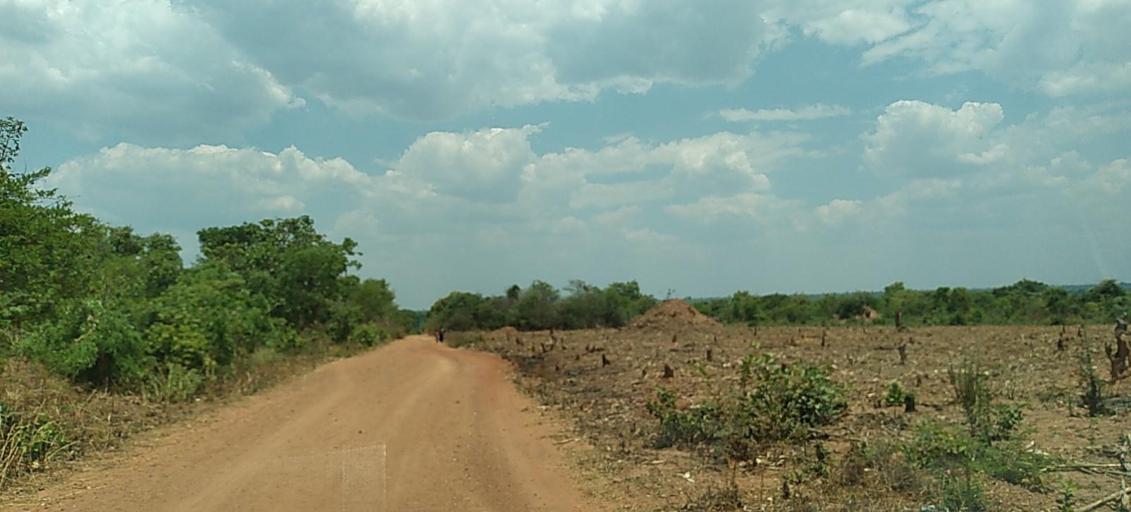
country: ZM
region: Copperbelt
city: Luanshya
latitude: -13.3853
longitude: 28.4417
